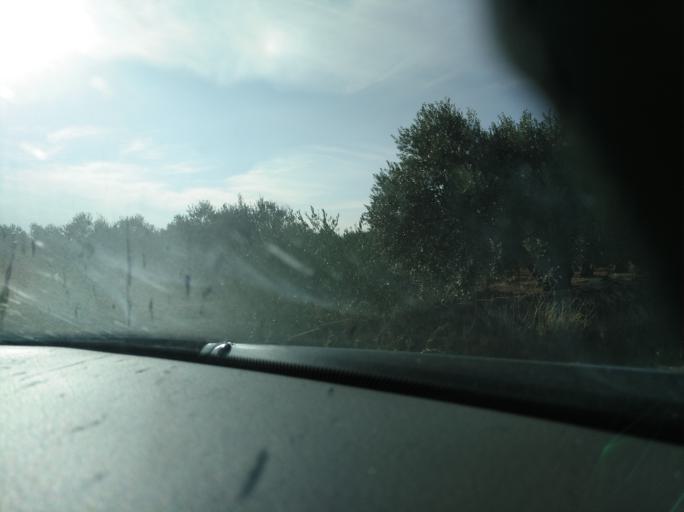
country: PT
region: Portalegre
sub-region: Elvas
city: Elvas
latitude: 38.8684
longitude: -7.2783
